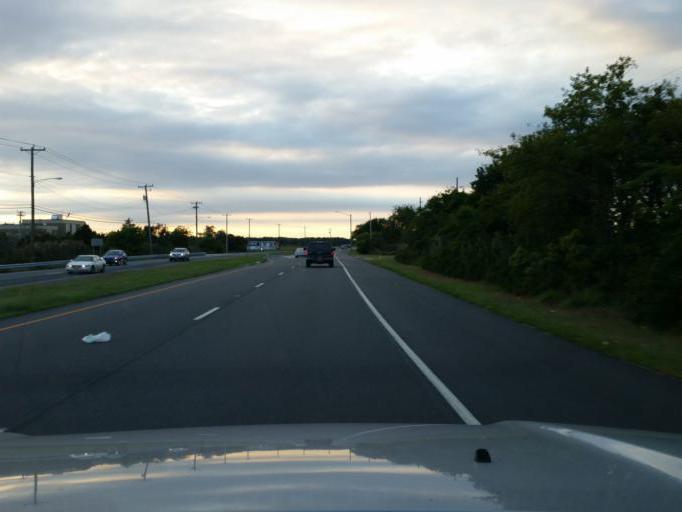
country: US
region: New Jersey
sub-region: Cape May County
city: Wildwood Crest
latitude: 38.9989
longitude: -74.8510
